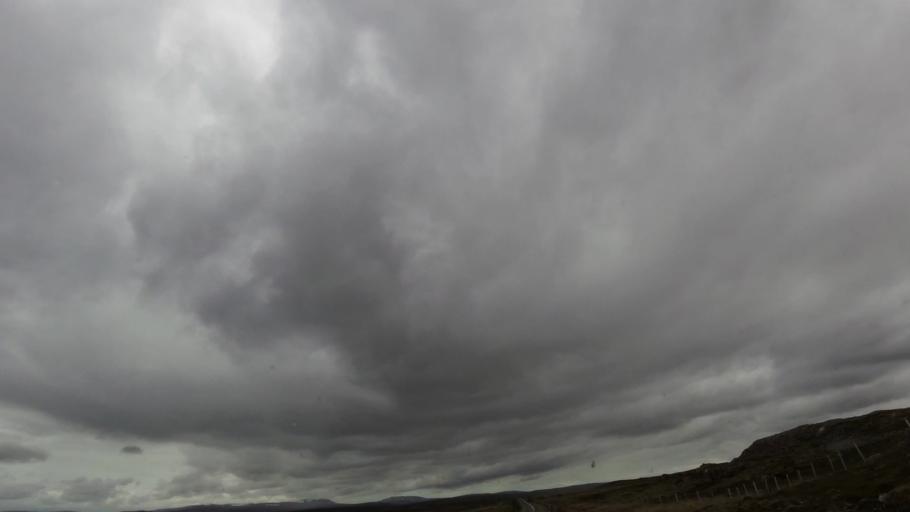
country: IS
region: West
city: Borgarnes
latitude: 65.1268
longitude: -21.7381
